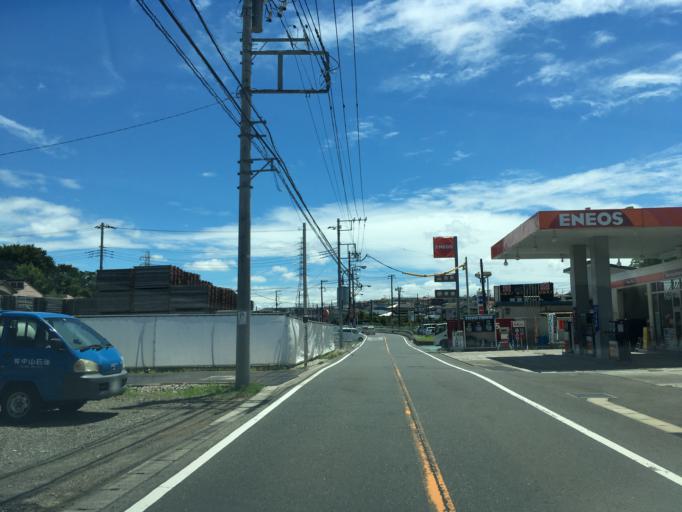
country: JP
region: Tokyo
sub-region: Machida-shi
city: Machida
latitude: 35.5481
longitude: 139.4911
